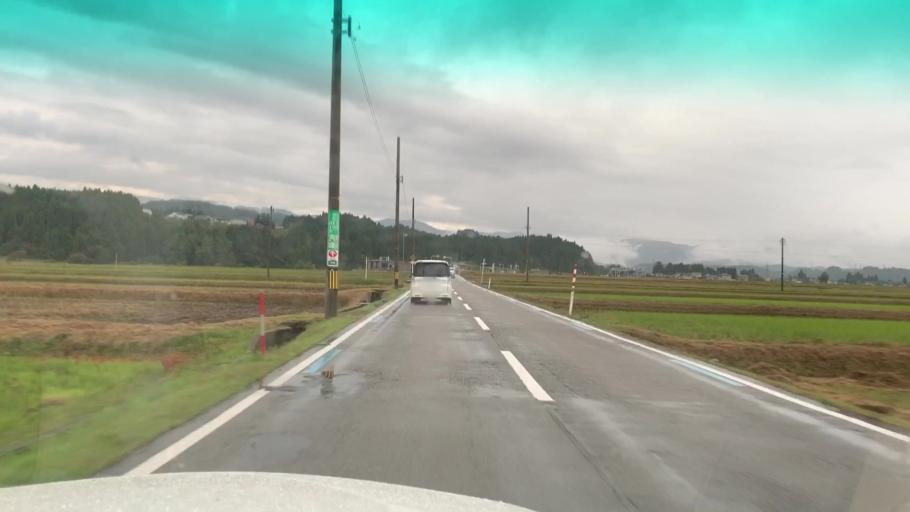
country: JP
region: Toyama
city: Kamiichi
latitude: 36.6245
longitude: 137.3286
